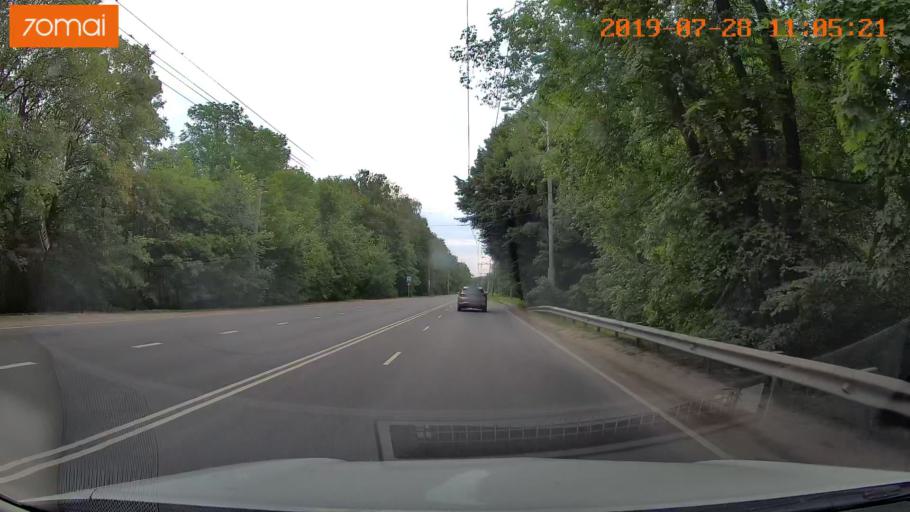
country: RU
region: Kaliningrad
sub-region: Gorod Kaliningrad
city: Kaliningrad
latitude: 54.7185
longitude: 20.3912
